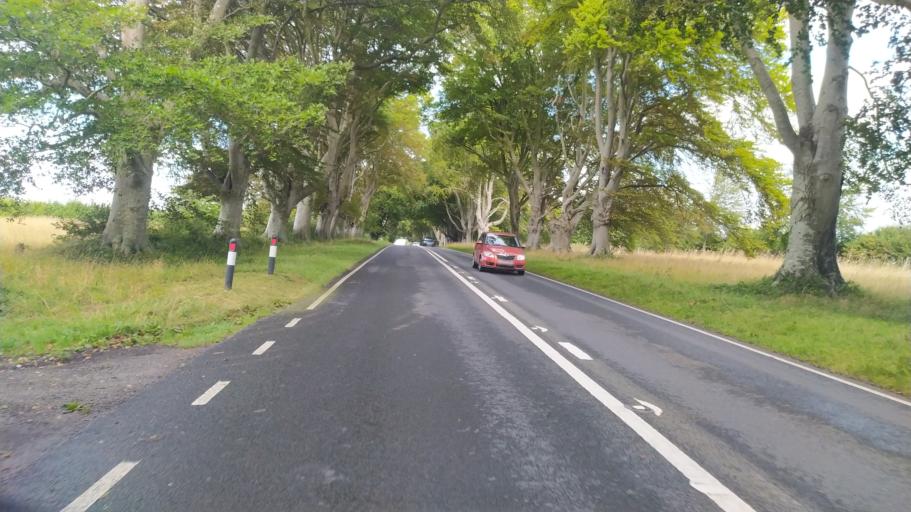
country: GB
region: England
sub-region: Dorset
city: Lytchett Matravers
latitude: 50.8316
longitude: -2.0747
